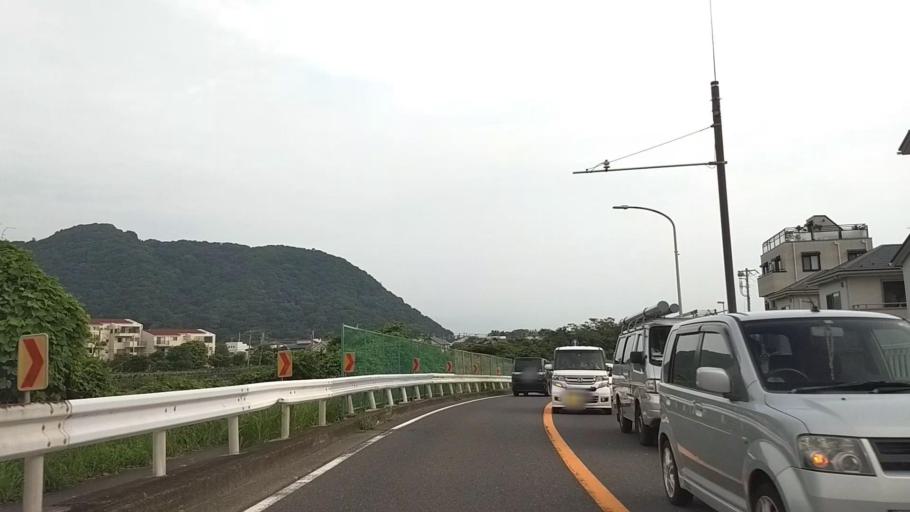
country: JP
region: Kanagawa
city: Hiratsuka
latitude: 35.3170
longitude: 139.3306
